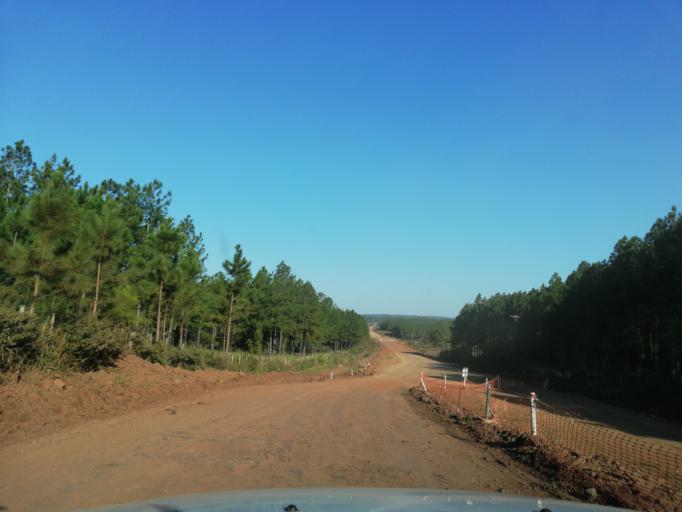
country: AR
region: Misiones
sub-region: Departamento de Candelaria
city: Candelaria
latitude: -27.5222
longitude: -55.7247
